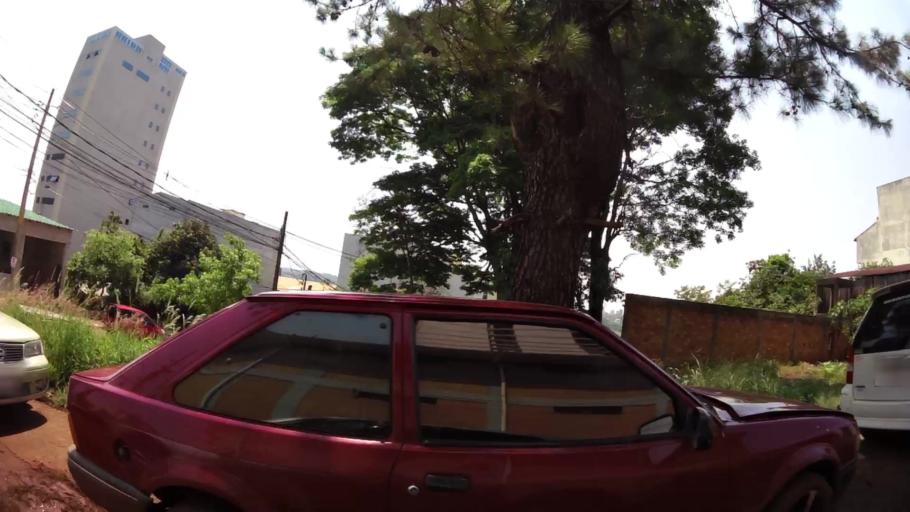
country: PY
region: Alto Parana
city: Ciudad del Este
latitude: -25.5142
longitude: -54.6079
